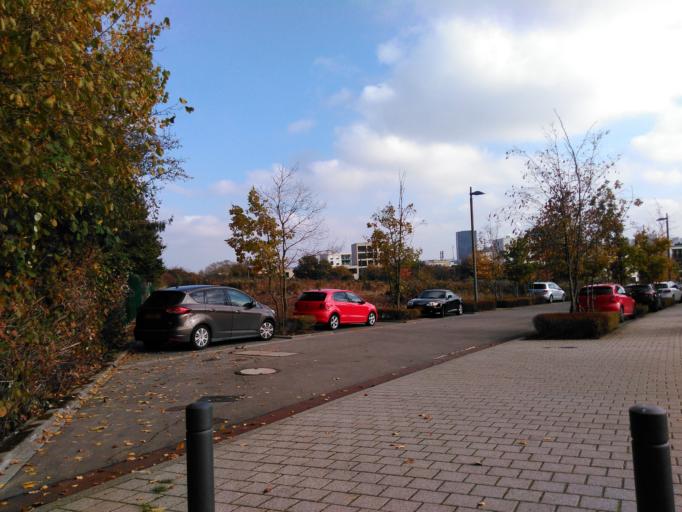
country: LU
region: Luxembourg
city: Belvaux
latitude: 49.5096
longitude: 5.9331
